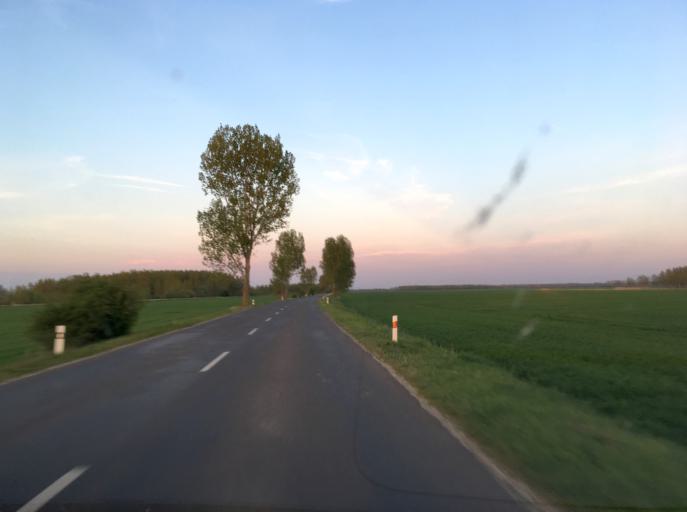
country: SK
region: Nitriansky
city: Kolarovo
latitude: 47.9178
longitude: 18.0610
